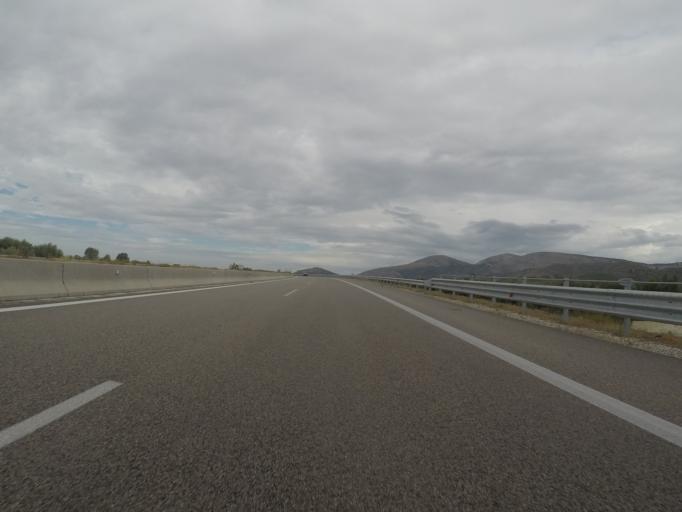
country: GR
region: West Greece
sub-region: Nomos Aitolias kai Akarnanias
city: Mesolongi
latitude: 38.3931
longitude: 21.4422
